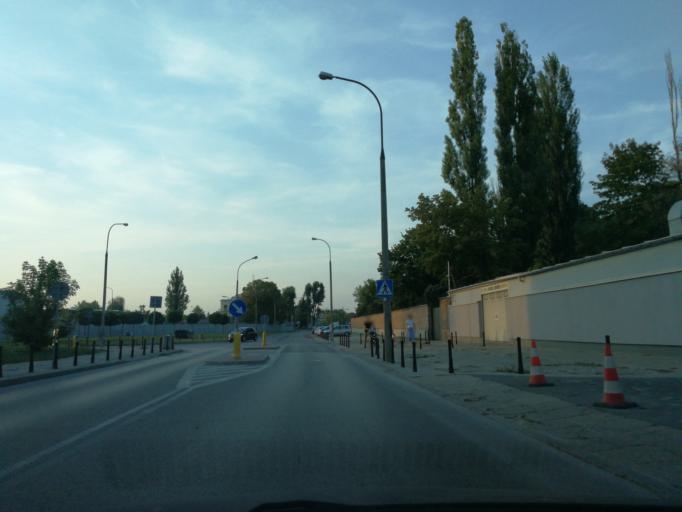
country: PL
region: Masovian Voivodeship
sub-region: Warszawa
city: Wola
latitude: 52.2471
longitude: 20.9661
